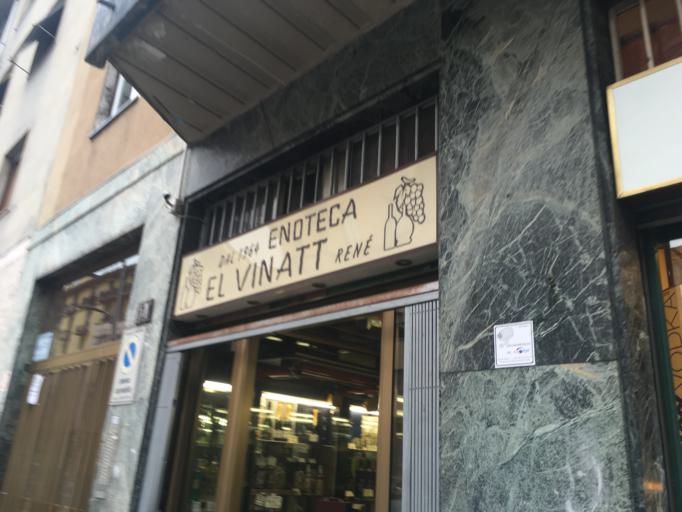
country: IT
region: Lombardy
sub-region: Citta metropolitana di Milano
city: Romano Banco
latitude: 45.4534
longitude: 9.1497
